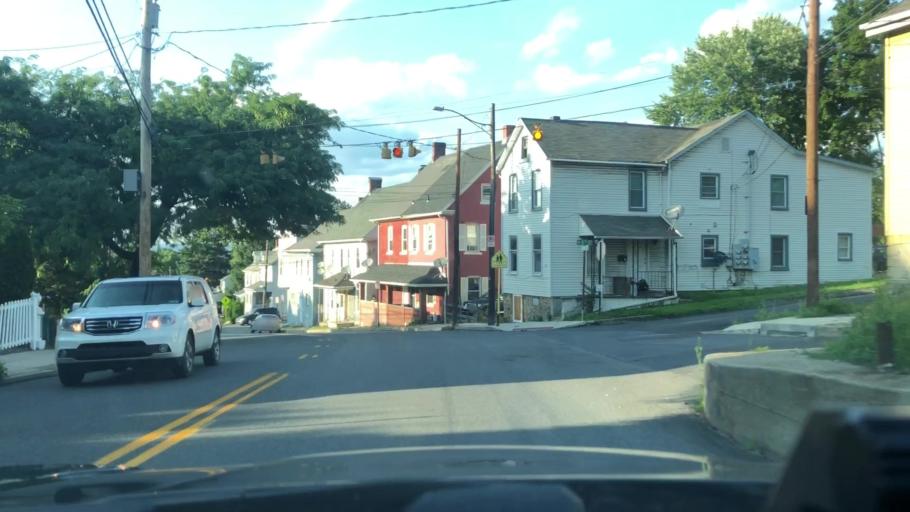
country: US
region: Pennsylvania
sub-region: Lehigh County
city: Fountain Hill
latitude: 40.6045
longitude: -75.3849
